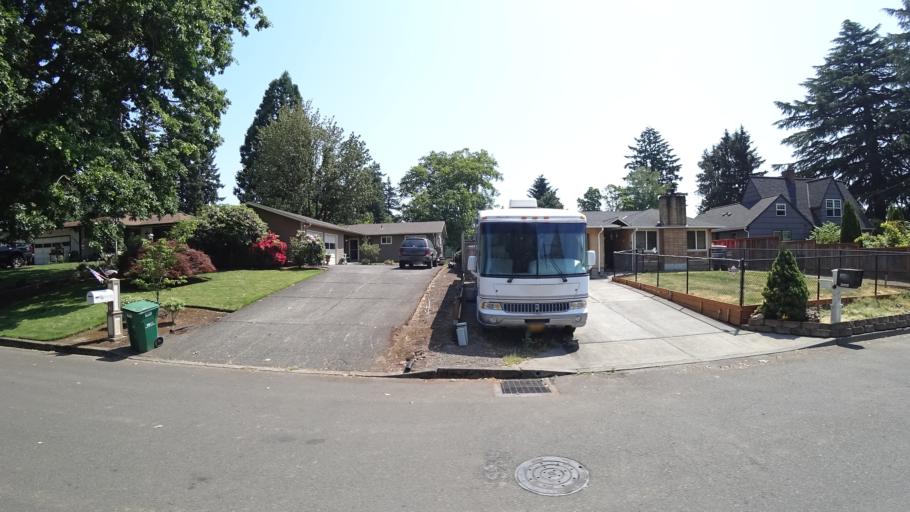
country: US
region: Oregon
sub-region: Clackamas County
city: Oatfield
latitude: 45.4440
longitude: -122.5842
